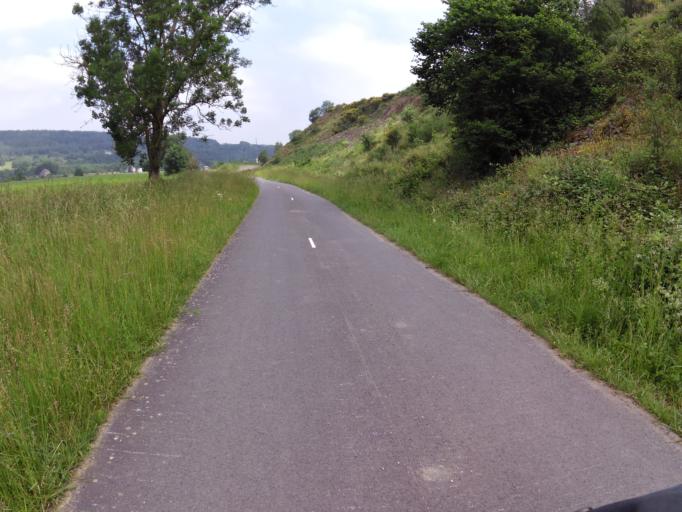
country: BE
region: Wallonia
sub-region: Province de Namur
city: Doische
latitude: 50.1063
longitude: 4.7687
